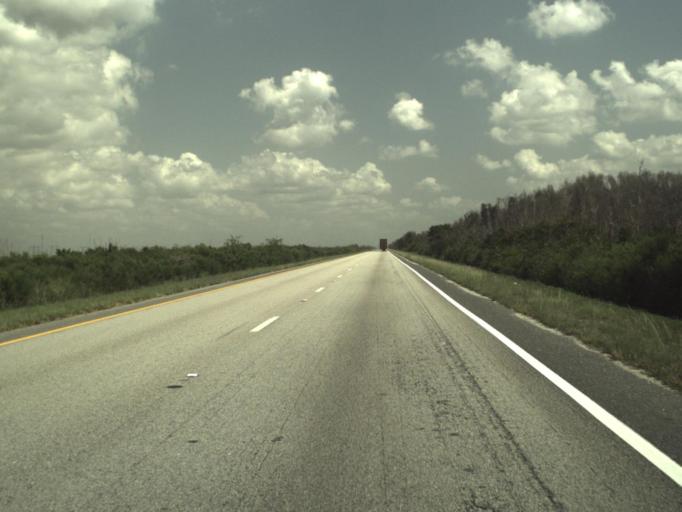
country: US
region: Florida
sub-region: Miami-Dade County
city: Palm Springs North
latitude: 25.9651
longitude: -80.4311
